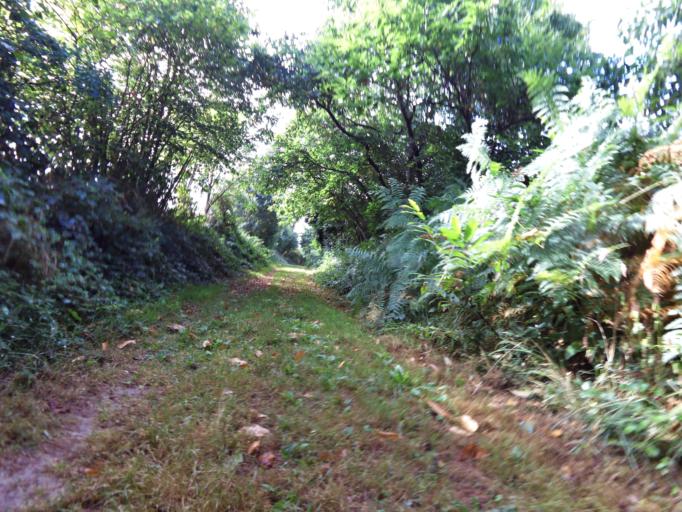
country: FR
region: Brittany
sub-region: Departement d'Ille-et-Vilaine
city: Chanteloup
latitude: 47.9294
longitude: -1.6020
